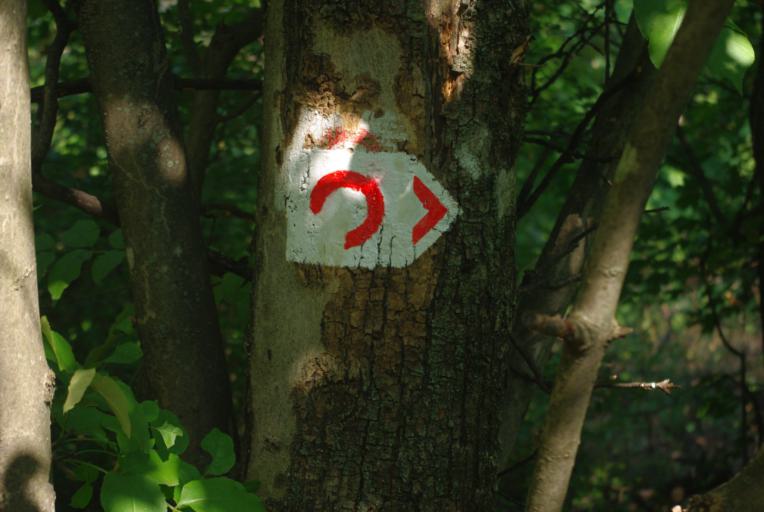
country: HU
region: Budapest
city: Budapest II. keruelet
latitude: 47.5425
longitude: 18.9811
